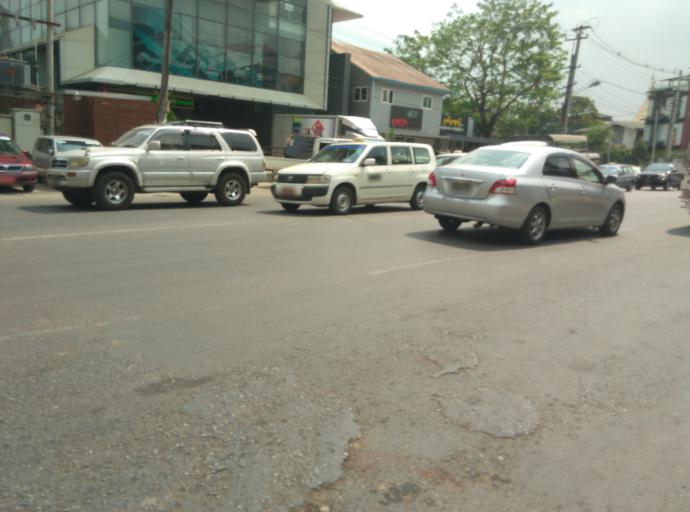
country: MM
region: Yangon
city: Yangon
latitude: 16.8056
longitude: 96.1545
